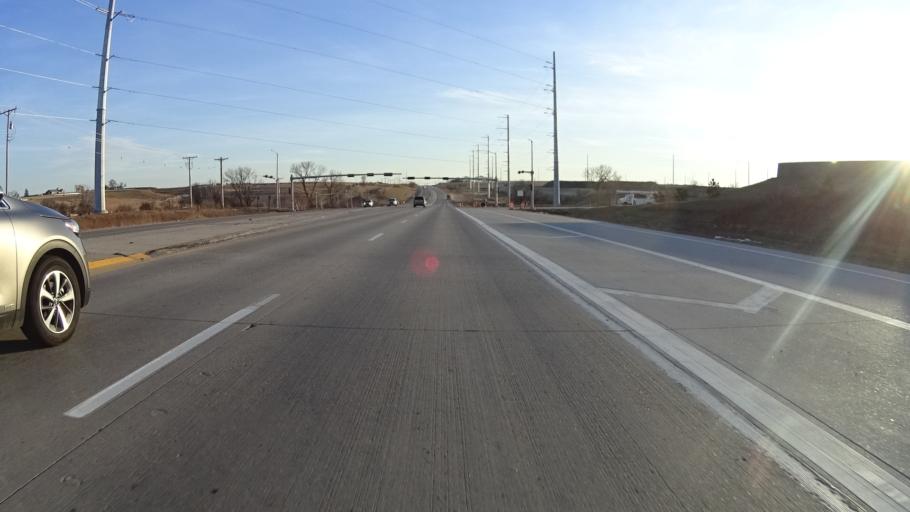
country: US
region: Nebraska
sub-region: Sarpy County
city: Chalco
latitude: 41.1412
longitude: -96.1391
